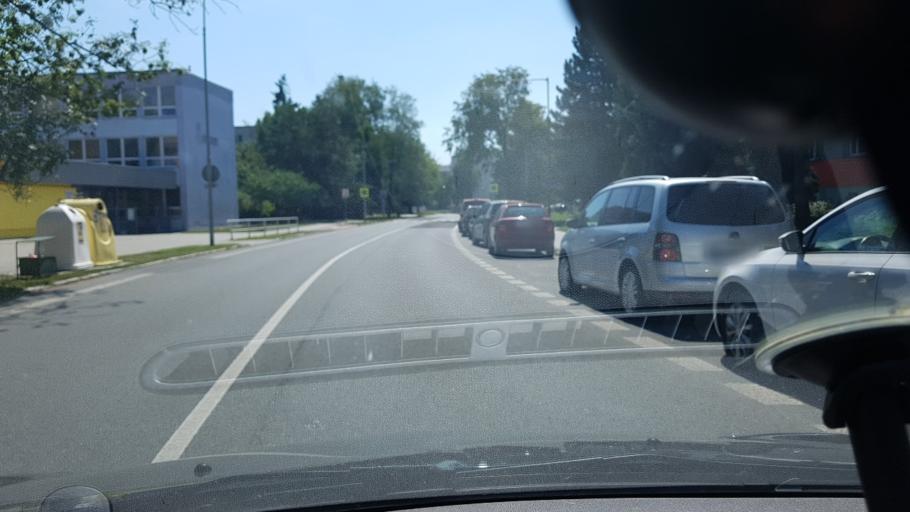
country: CZ
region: Moravskoslezsky
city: Bohumin
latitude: 49.9054
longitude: 18.3501
